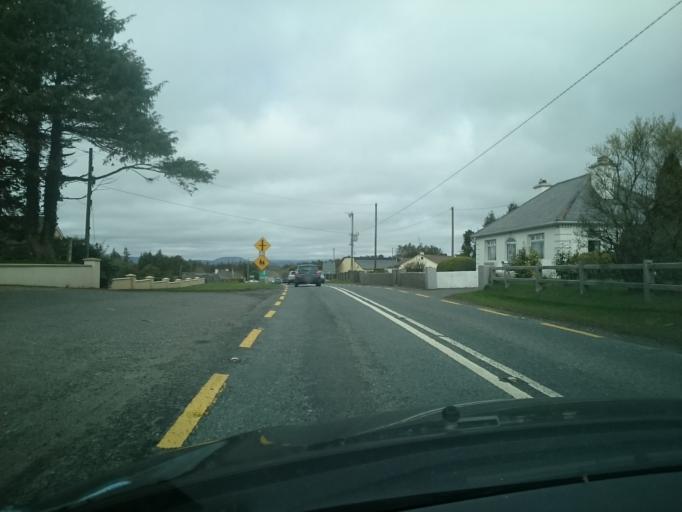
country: IE
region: Connaught
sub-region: Maigh Eo
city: Castlebar
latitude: 53.8312
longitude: -9.1828
